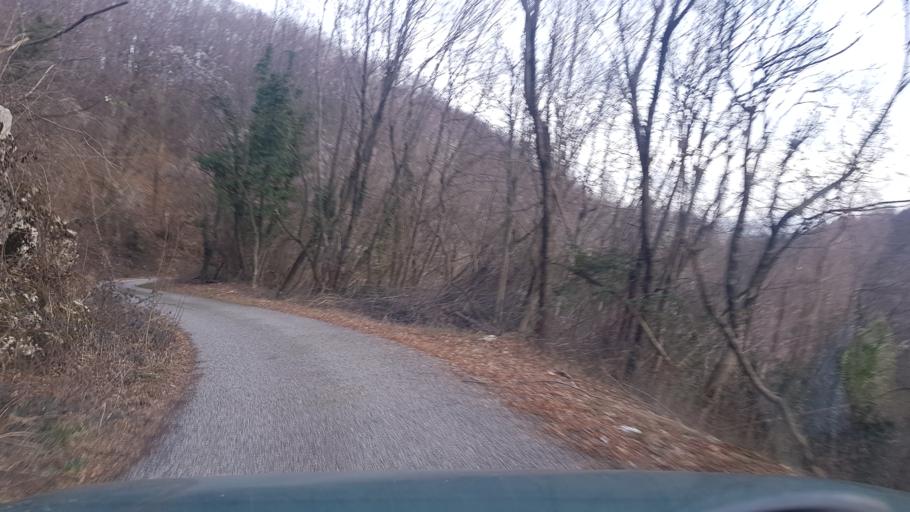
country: IT
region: Friuli Venezia Giulia
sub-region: Provincia di Udine
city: Pulfero
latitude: 46.1490
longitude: 13.4584
